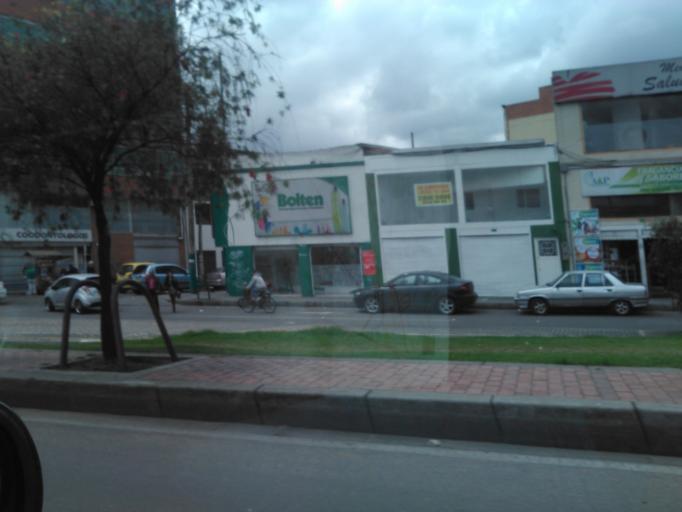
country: CO
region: Bogota D.C.
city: Bogota
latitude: 4.6281
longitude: -74.1173
